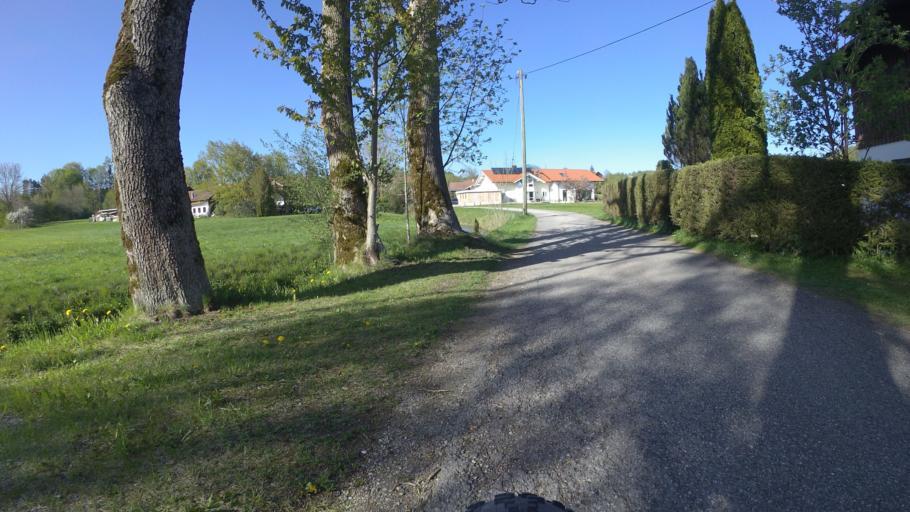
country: DE
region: Bavaria
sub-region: Upper Bavaria
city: Grabenstatt
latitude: 47.8501
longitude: 12.5603
